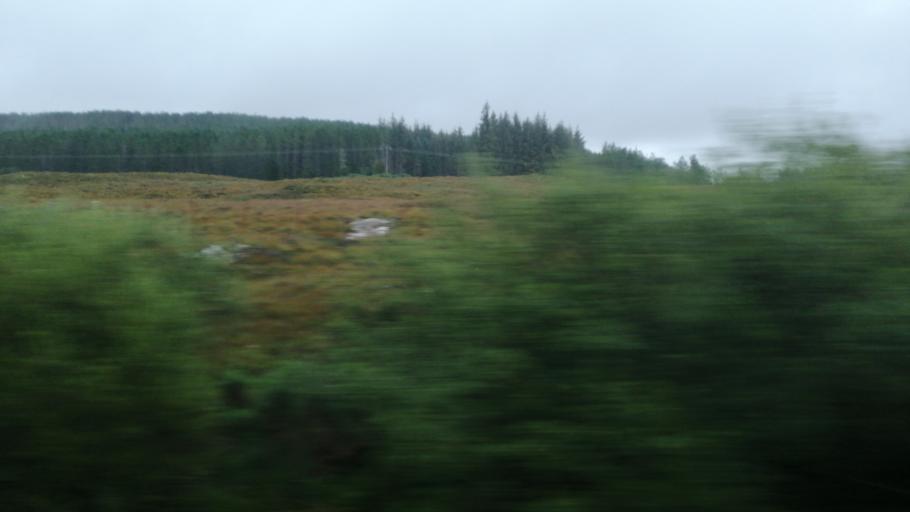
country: GB
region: Scotland
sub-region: Highland
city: Brora
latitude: 58.3315
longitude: -3.9144
